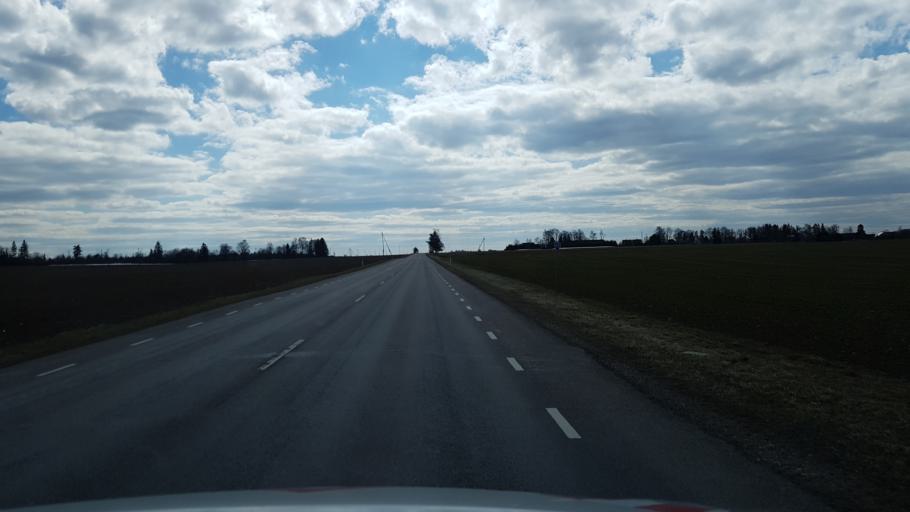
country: EE
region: Laeaene-Virumaa
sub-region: Vaeike-Maarja vald
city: Vaike-Maarja
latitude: 59.1875
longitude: 26.2655
